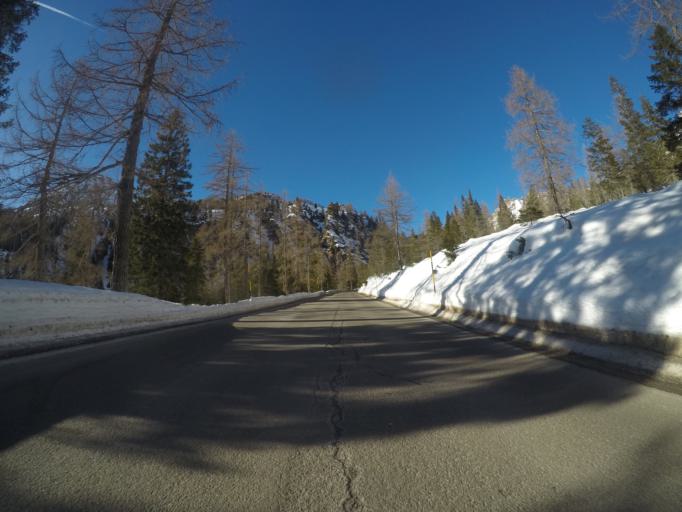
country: IT
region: Trentino-Alto Adige
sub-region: Provincia di Trento
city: Siror
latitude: 46.2783
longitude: 11.8008
